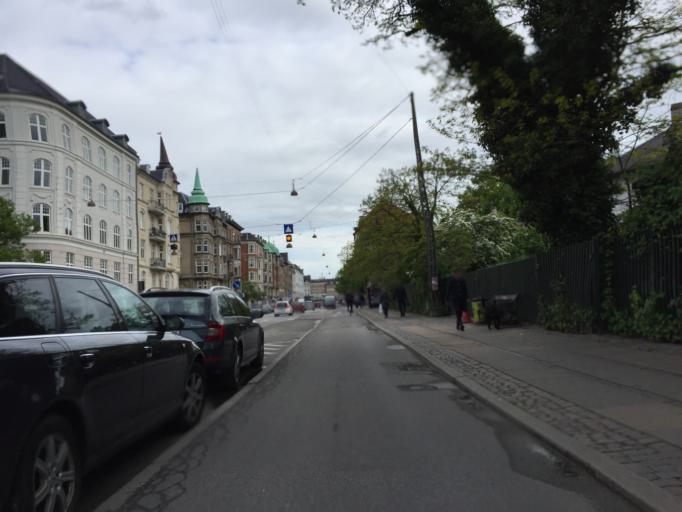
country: DK
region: Capital Region
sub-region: Kobenhavn
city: Copenhagen
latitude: 55.7029
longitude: 12.5773
